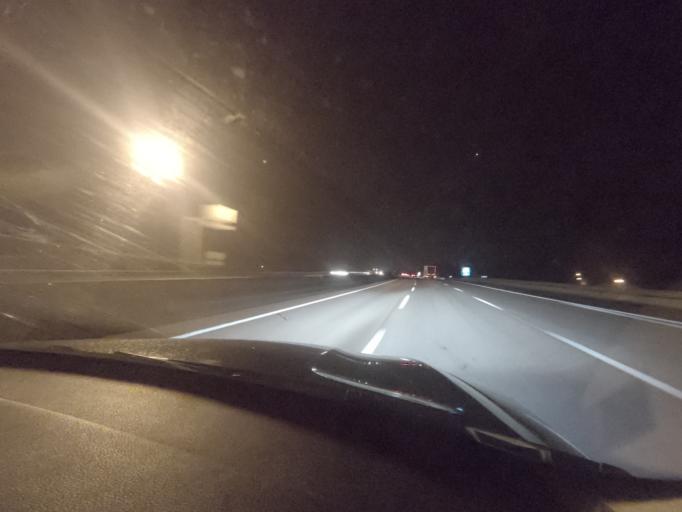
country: PT
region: Lisbon
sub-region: Azambuja
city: Aveiras de Cima
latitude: 39.1211
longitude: -8.9110
